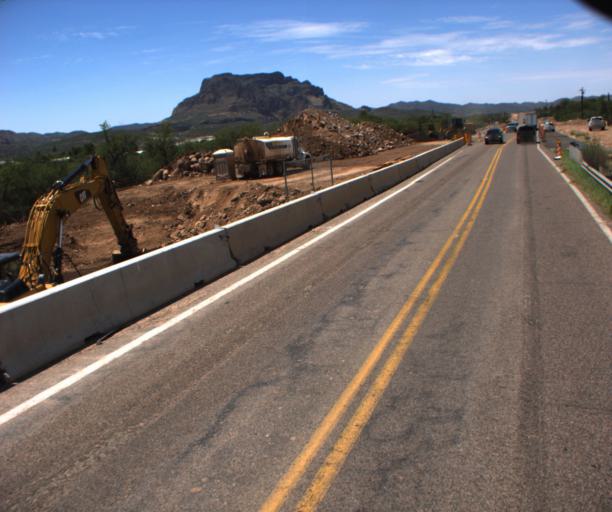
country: US
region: Arizona
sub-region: Pinal County
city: Superior
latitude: 33.2869
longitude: -111.1085
